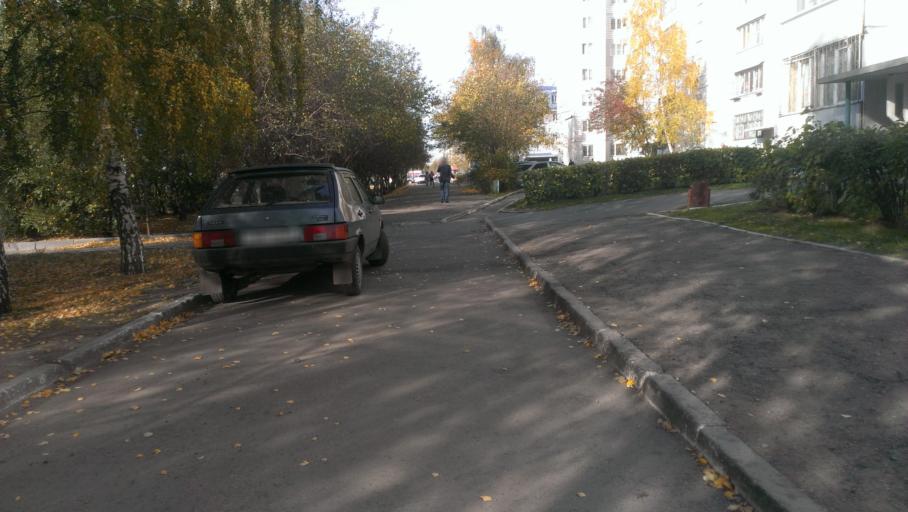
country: RU
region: Altai Krai
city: Novosilikatnyy
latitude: 53.3340
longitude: 83.6690
